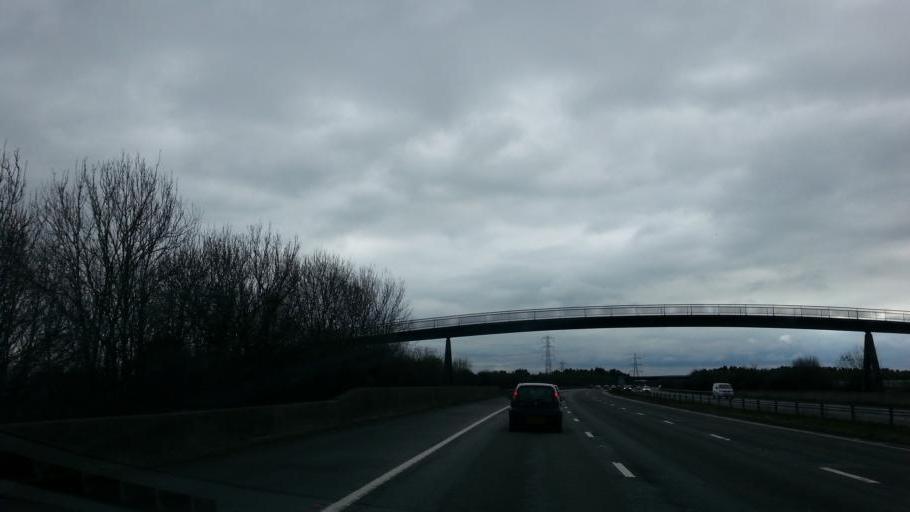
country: GB
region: England
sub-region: Somerset
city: Bridgwater
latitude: 51.1292
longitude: -2.9680
